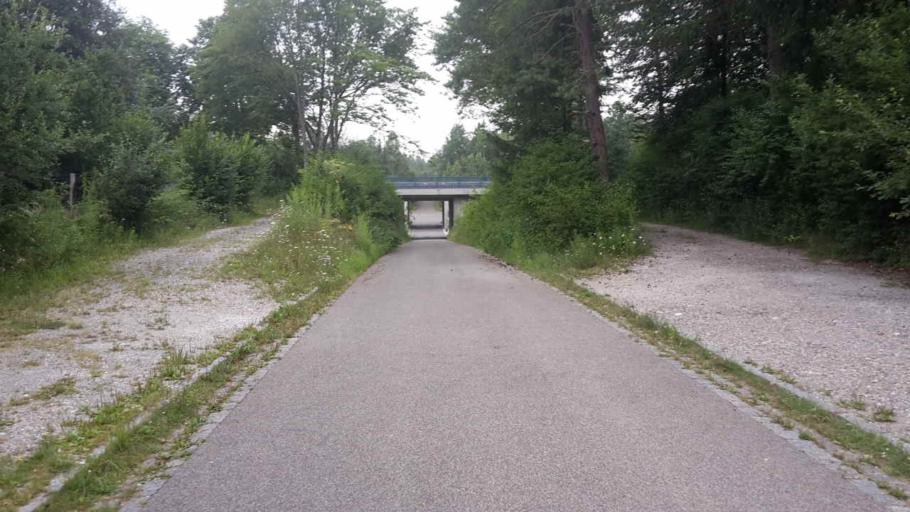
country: DE
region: Bavaria
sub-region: Upper Bavaria
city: Neuried
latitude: 48.0606
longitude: 11.4747
